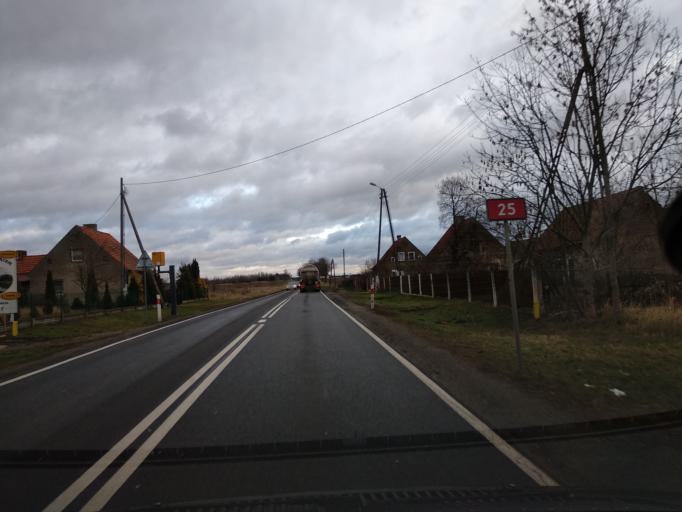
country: PL
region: Lower Silesian Voivodeship
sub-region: Powiat olesnicki
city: Miedzyborz
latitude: 51.3402
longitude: 17.5861
